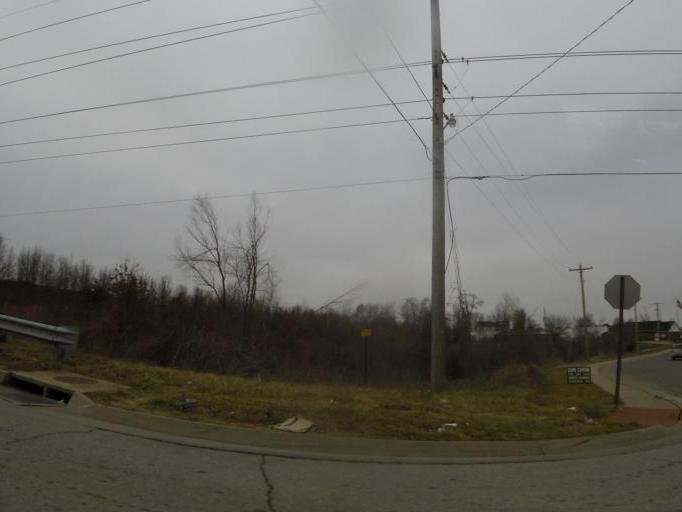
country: US
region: Missouri
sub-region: Marion County
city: Hannibal
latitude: 39.7253
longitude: -91.3970
